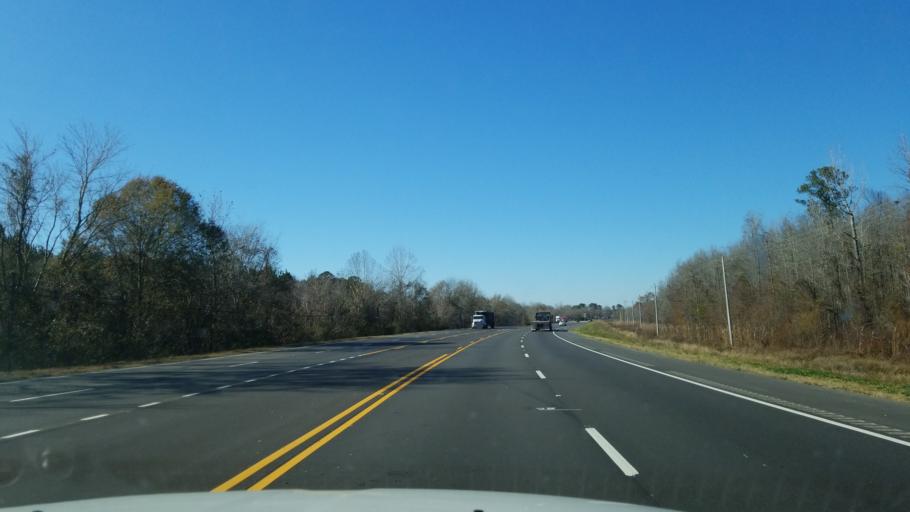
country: US
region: Alabama
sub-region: Pickens County
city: Reform
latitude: 33.3721
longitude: -87.9989
